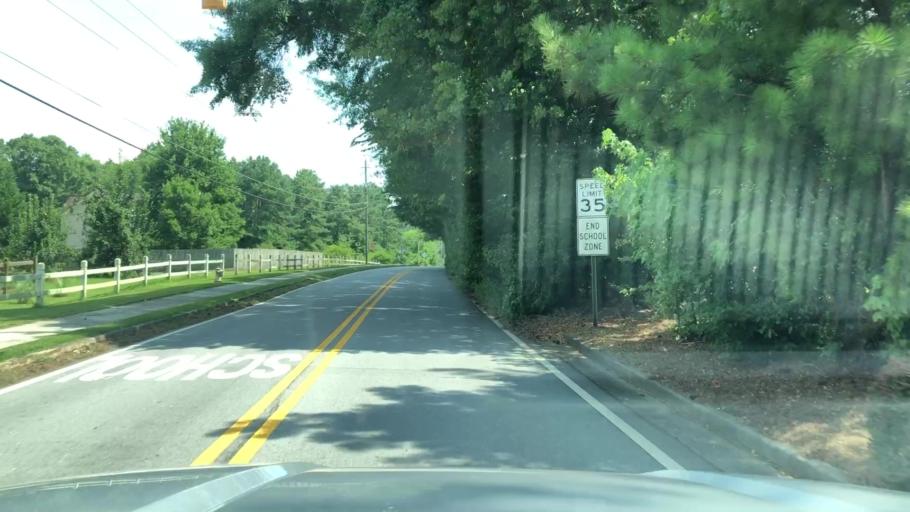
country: US
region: Georgia
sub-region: Paulding County
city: Hiram
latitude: 33.9577
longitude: -84.7258
